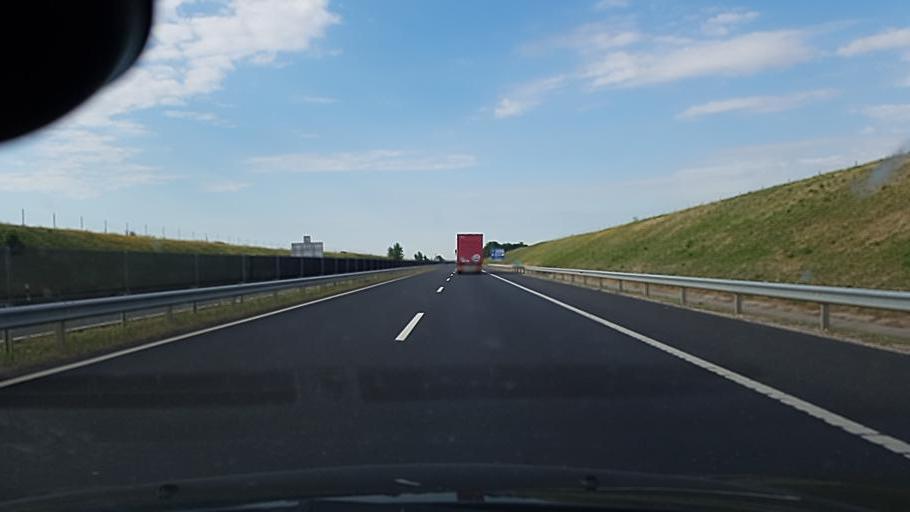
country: HU
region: Fejer
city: Rackeresztur
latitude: 47.3007
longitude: 18.8661
